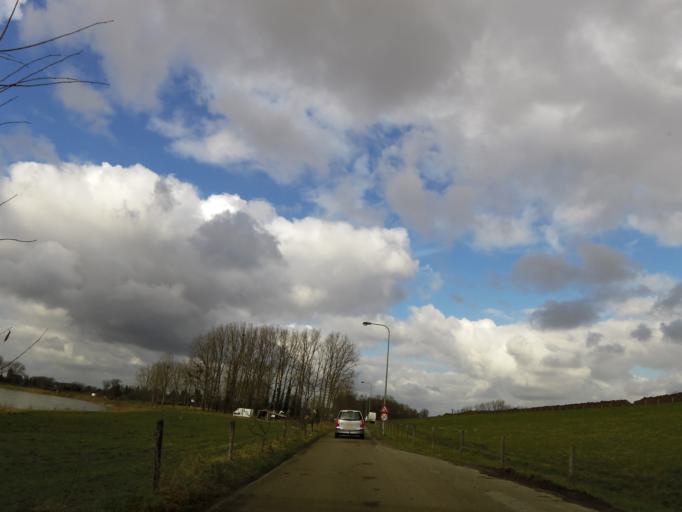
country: NL
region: Limburg
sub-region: Gemeente Stein
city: Stein
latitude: 50.9602
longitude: 5.7529
